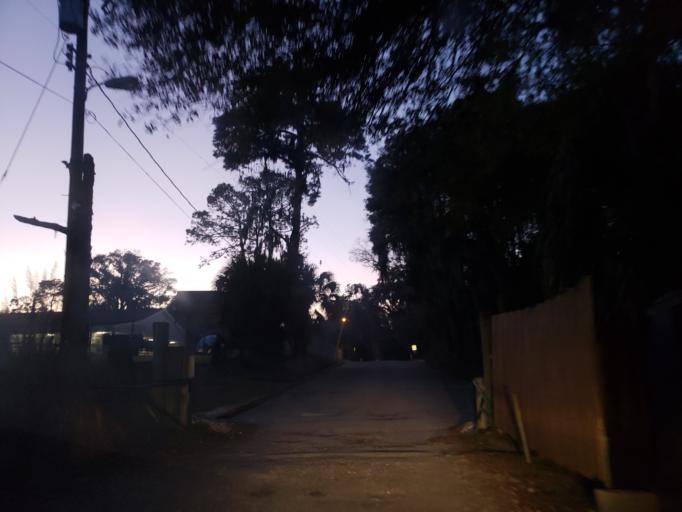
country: US
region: Georgia
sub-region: Chatham County
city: Thunderbolt
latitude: 32.0140
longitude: -81.0605
